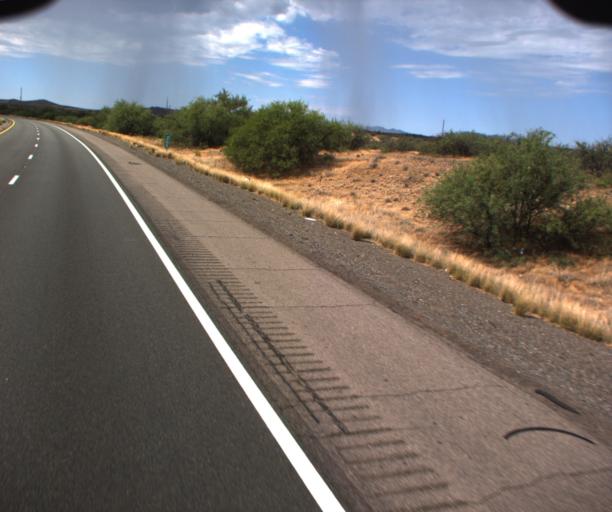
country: US
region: Arizona
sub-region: Yavapai County
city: Spring Valley
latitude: 34.3631
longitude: -112.1166
